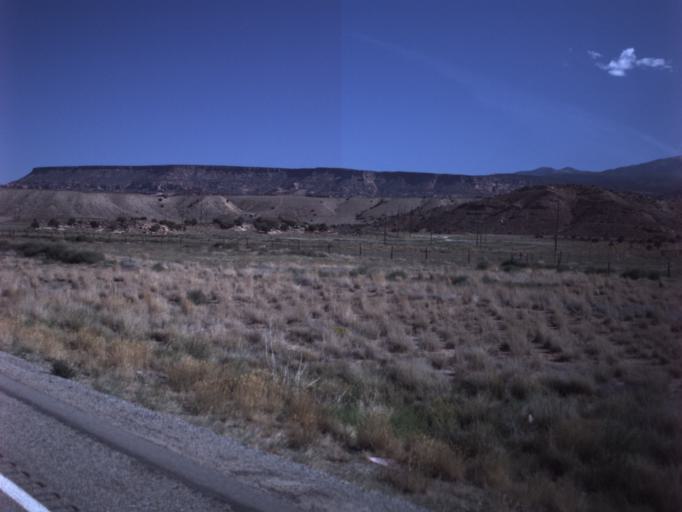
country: US
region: Utah
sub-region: Grand County
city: Moab
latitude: 38.4363
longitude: -109.4284
